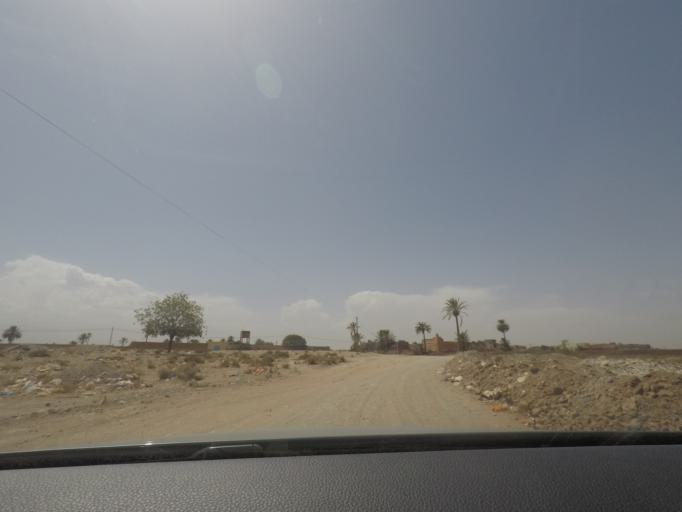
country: MA
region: Marrakech-Tensift-Al Haouz
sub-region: Marrakech
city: Marrakesh
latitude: 31.5831
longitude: -8.0297
